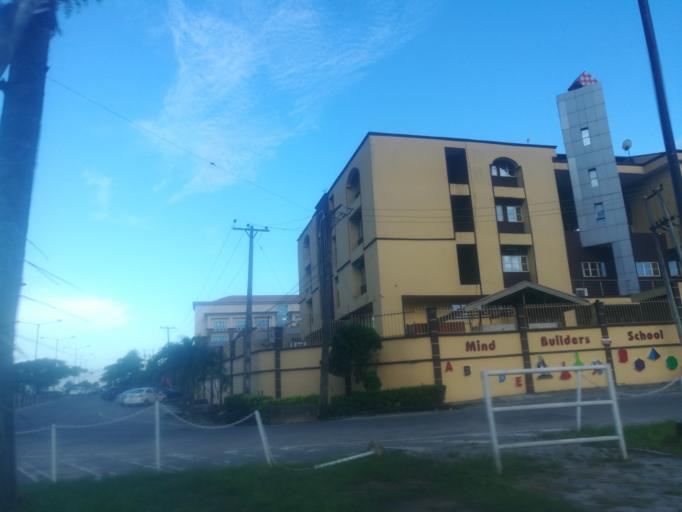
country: NG
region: Lagos
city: Ikeja
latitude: 6.6264
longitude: 3.3614
